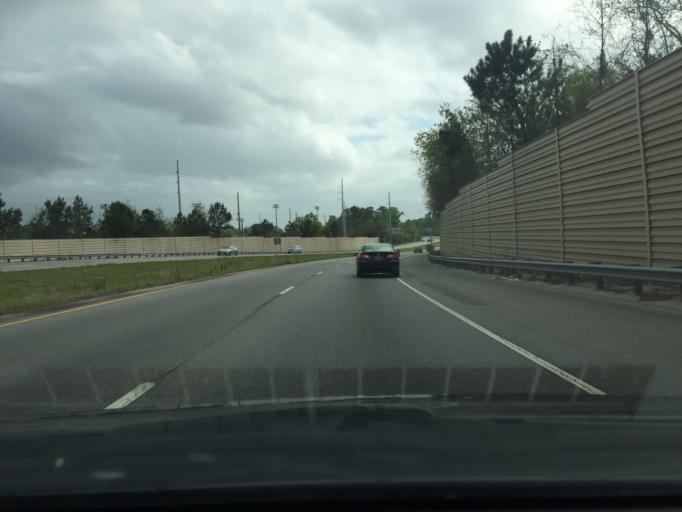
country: US
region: Georgia
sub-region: Chatham County
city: Isle of Hope
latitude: 31.9989
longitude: -81.0802
